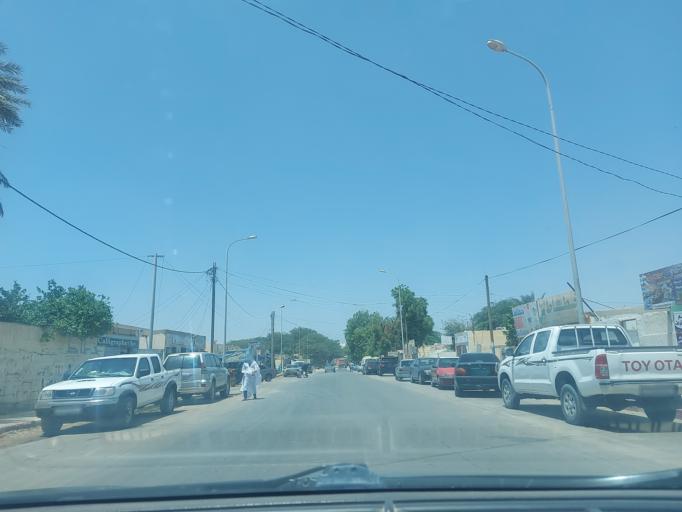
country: MR
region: Nouakchott
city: Nouakchott
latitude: 18.0892
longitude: -15.9805
